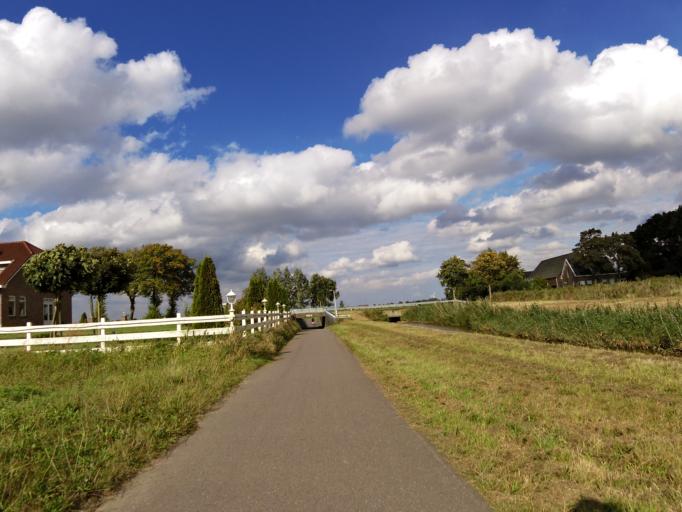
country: NL
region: South Holland
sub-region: Gemeente Waddinxveen
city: Groenswaard
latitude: 52.0762
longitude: 4.6068
